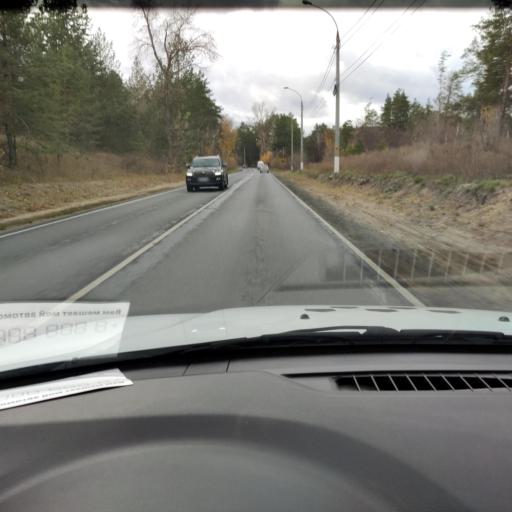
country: RU
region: Samara
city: Zhigulevsk
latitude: 53.4782
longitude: 49.4417
